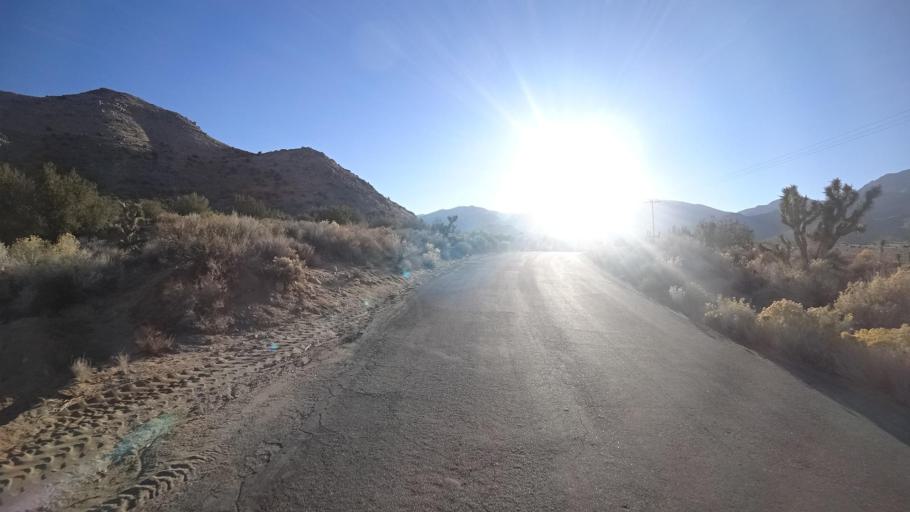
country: US
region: California
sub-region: Kern County
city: Weldon
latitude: 35.5829
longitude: -118.2462
